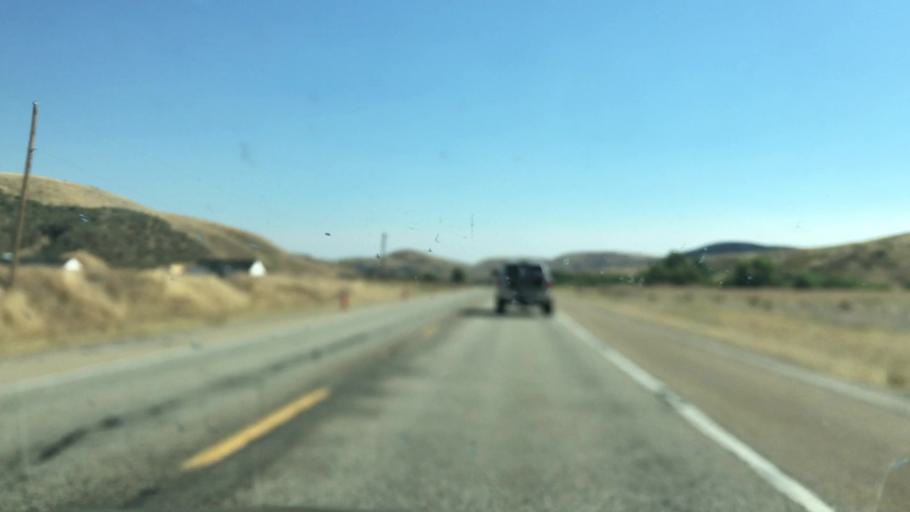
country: US
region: Idaho
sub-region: Ada County
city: Eagle
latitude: 43.7895
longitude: -116.2632
